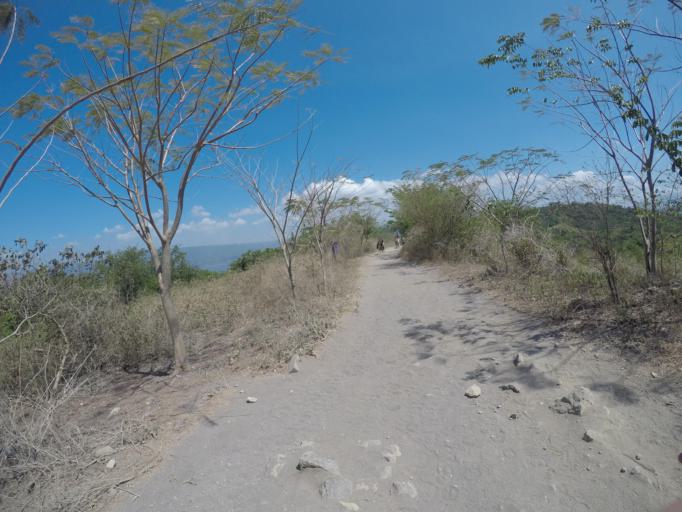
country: PH
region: Calabarzon
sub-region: Province of Batangas
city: Bugaan
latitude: 14.0221
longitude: 120.9994
